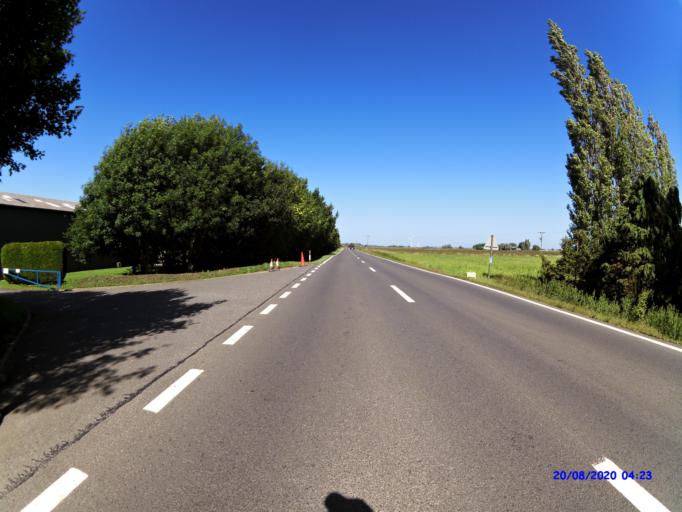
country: GB
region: England
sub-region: Cambridgeshire
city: Ramsey
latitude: 52.4988
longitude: -0.1268
